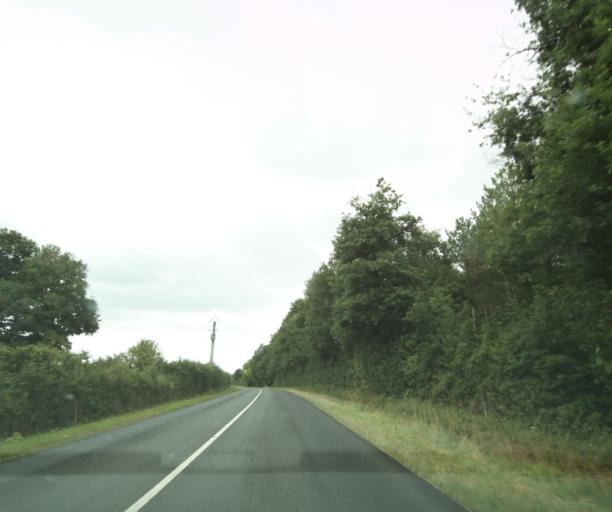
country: FR
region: Pays de la Loire
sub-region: Departement de la Sarthe
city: Precigne
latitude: 47.7914
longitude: -0.3206
